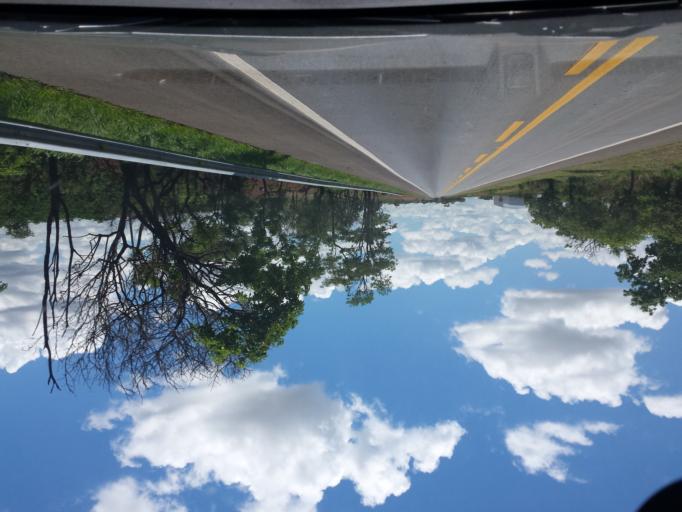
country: BR
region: Goias
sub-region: Cristalina
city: Cristalina
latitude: -16.6613
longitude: -47.7231
